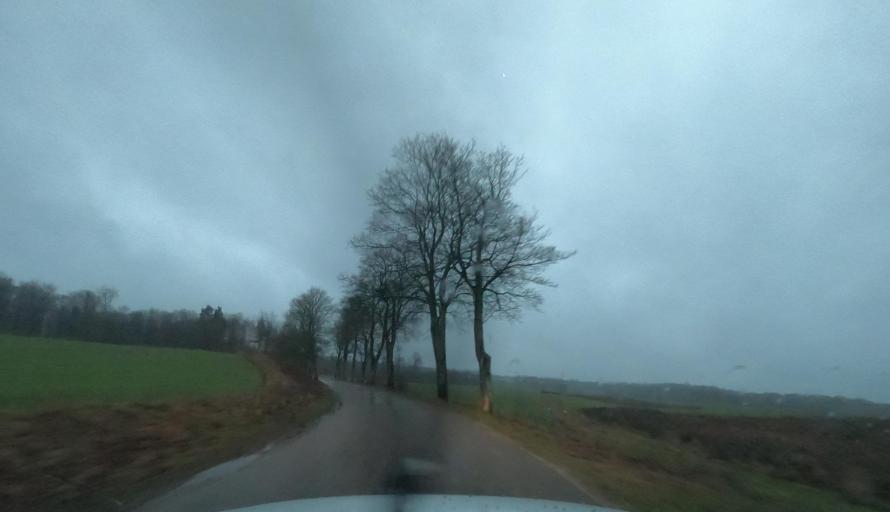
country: PL
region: West Pomeranian Voivodeship
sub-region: Powiat szczecinecki
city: Borne Sulinowo
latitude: 53.6611
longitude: 16.4877
